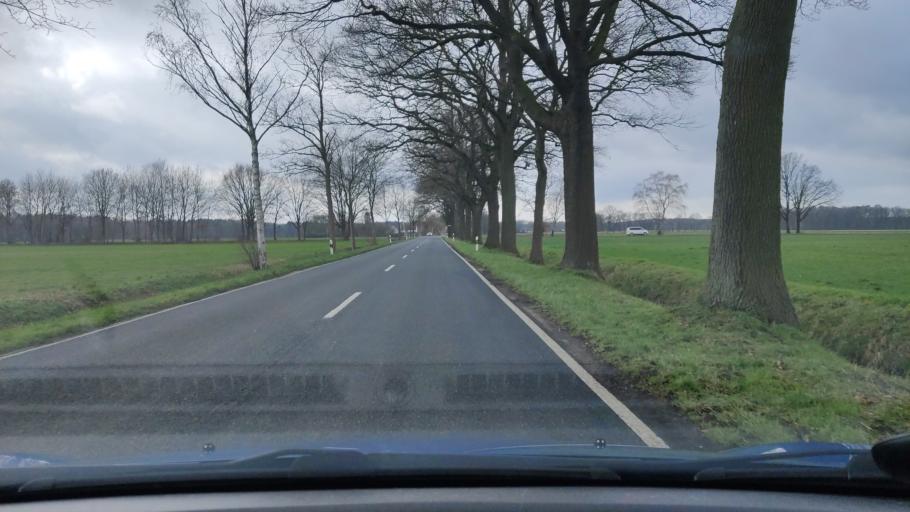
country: DE
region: Lower Saxony
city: Langenhagen
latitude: 52.4771
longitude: 9.7026
